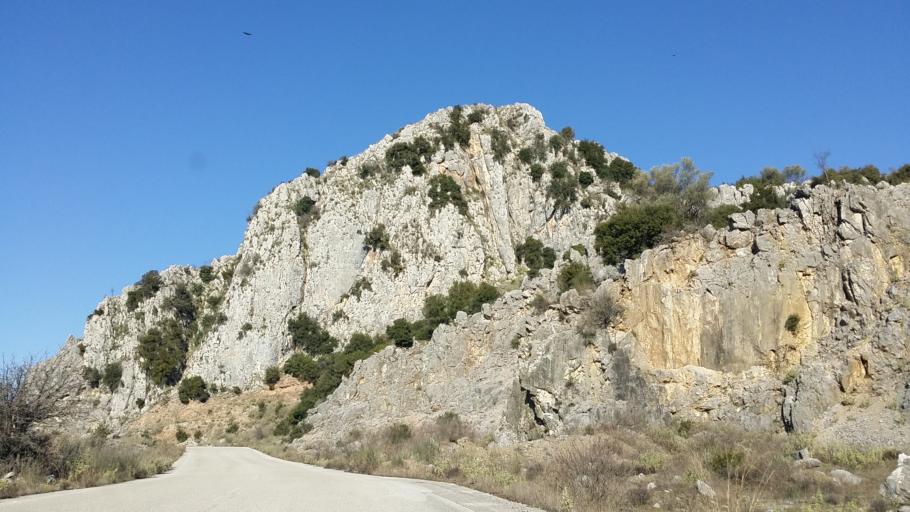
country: GR
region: West Greece
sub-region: Nomos Aitolias kai Akarnanias
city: Sardinia
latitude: 38.9242
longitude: 21.4068
